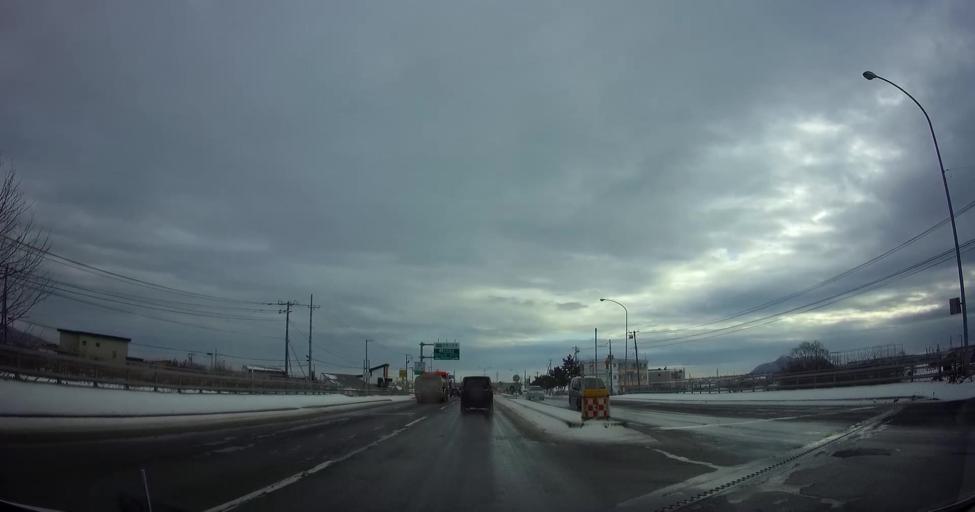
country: JP
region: Hokkaido
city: Nanae
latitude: 41.8386
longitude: 140.6903
